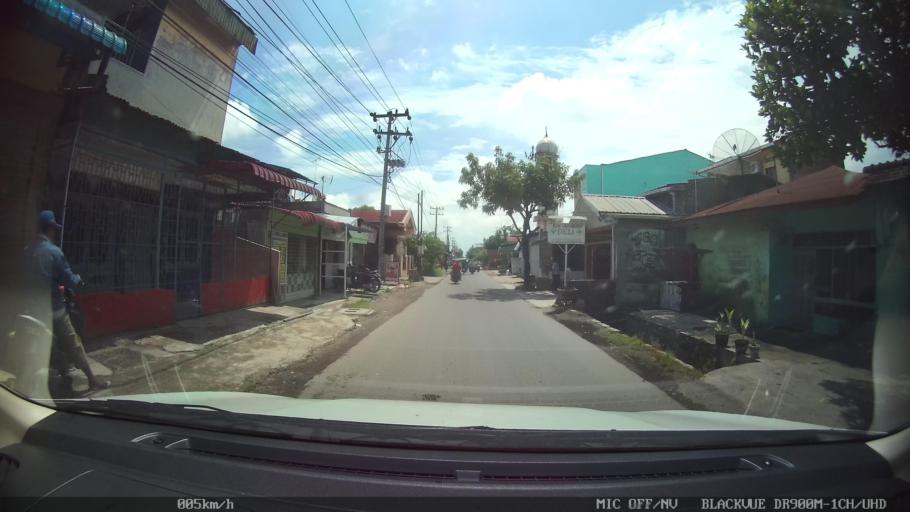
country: ID
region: North Sumatra
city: Medan
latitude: 3.6021
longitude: 98.7578
